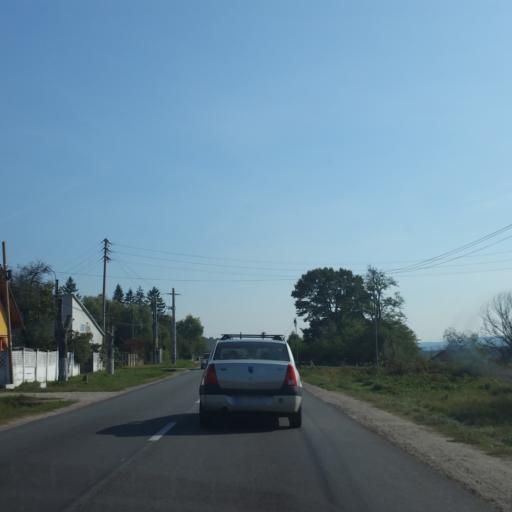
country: RO
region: Arges
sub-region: Comuna Baiculesti
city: Baiculesti
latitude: 45.0450
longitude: 24.7005
